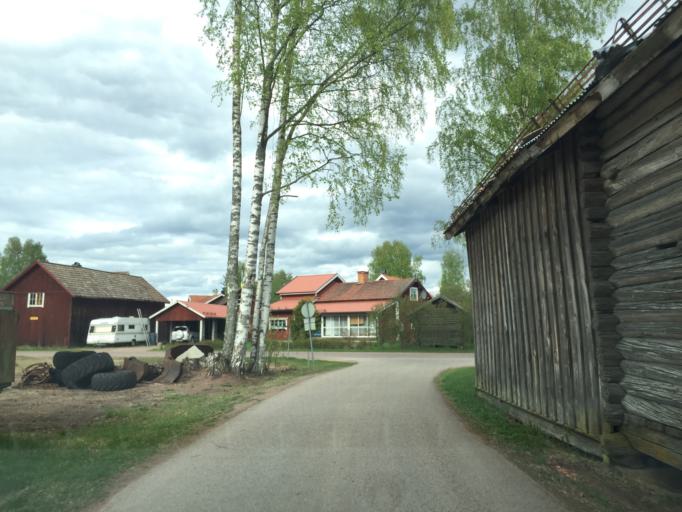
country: SE
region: Dalarna
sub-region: Mora Kommun
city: Mora
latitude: 61.0323
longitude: 14.5251
